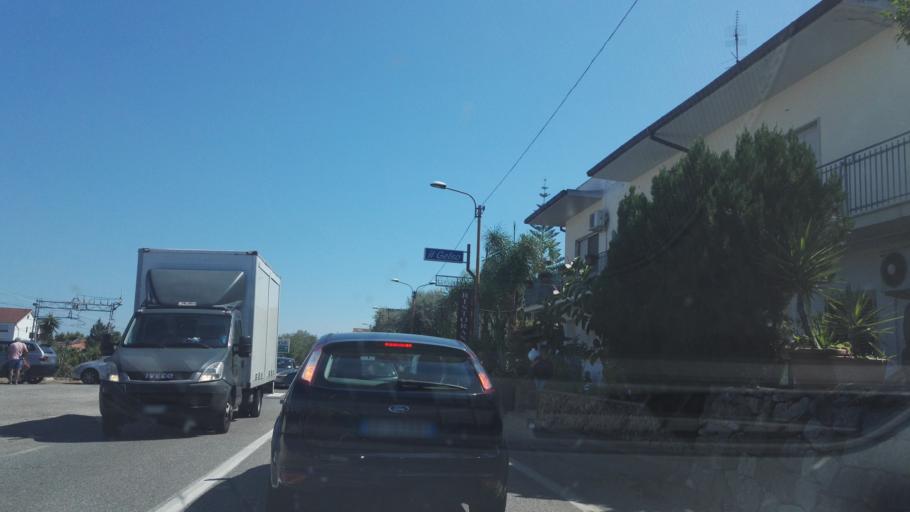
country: IT
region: Calabria
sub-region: Provincia di Cosenza
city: Borgata Marina
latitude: 39.9760
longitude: 16.6176
